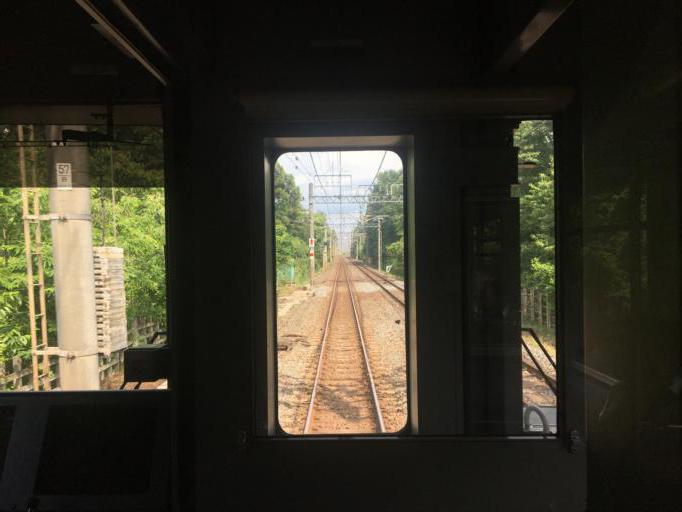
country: JP
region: Saitama
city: Sakado
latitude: 36.0439
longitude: 139.3806
